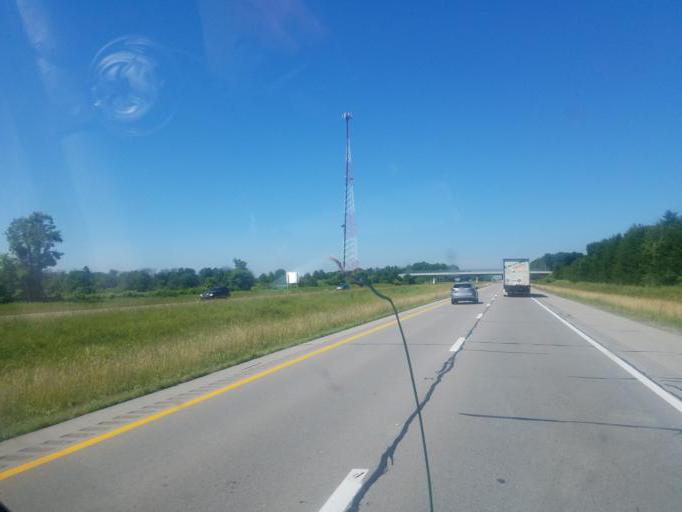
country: US
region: Ohio
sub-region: Clinton County
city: Wilmington
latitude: 39.5031
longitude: -83.8918
